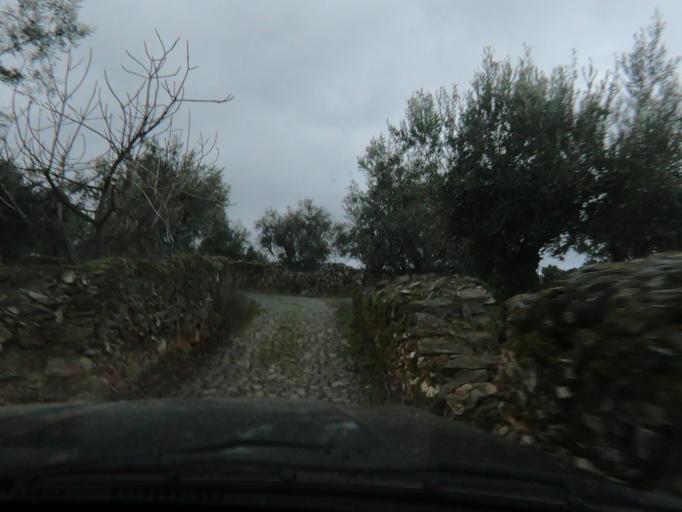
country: PT
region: Vila Real
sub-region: Vila Real
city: Vila Real
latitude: 41.2509
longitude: -7.7380
